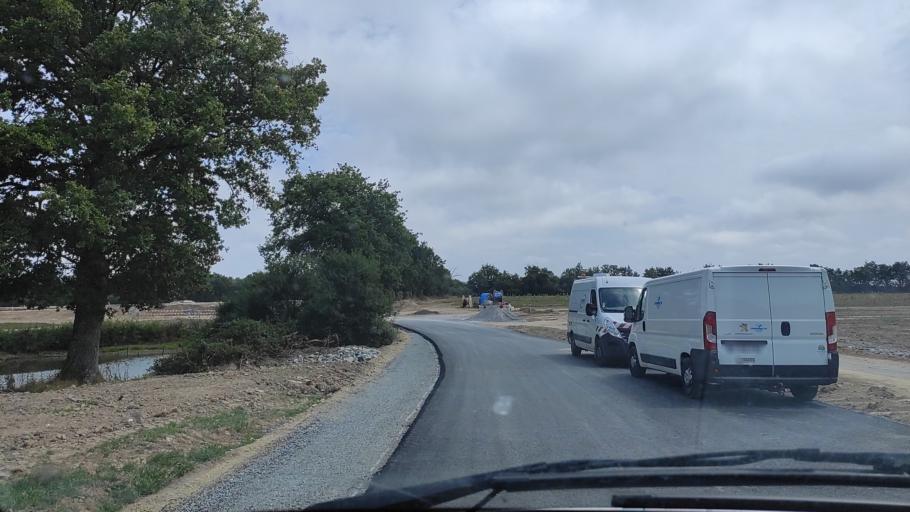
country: FR
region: Pays de la Loire
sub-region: Departement de la Vendee
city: Dompierre-sur-Yon
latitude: 46.7399
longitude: -1.4195
